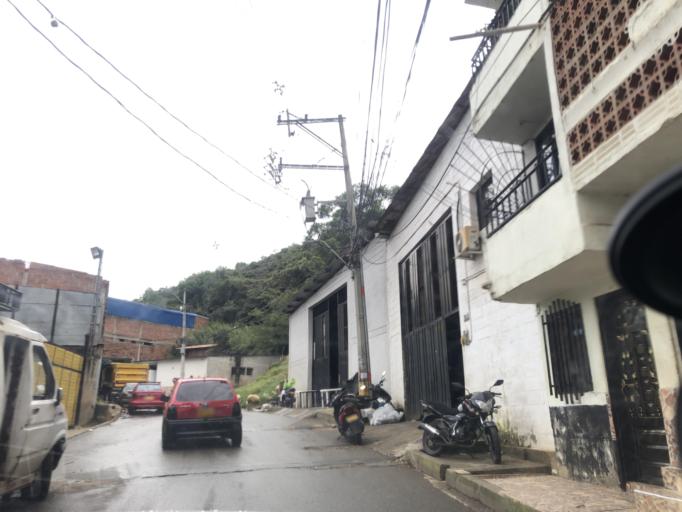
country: CO
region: Antioquia
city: Bello
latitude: 6.3246
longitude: -75.5470
